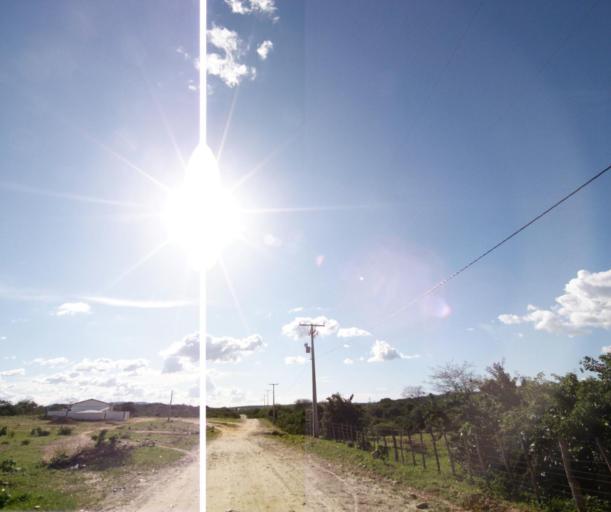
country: BR
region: Bahia
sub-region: Tanhacu
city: Tanhacu
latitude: -14.1822
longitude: -41.0064
